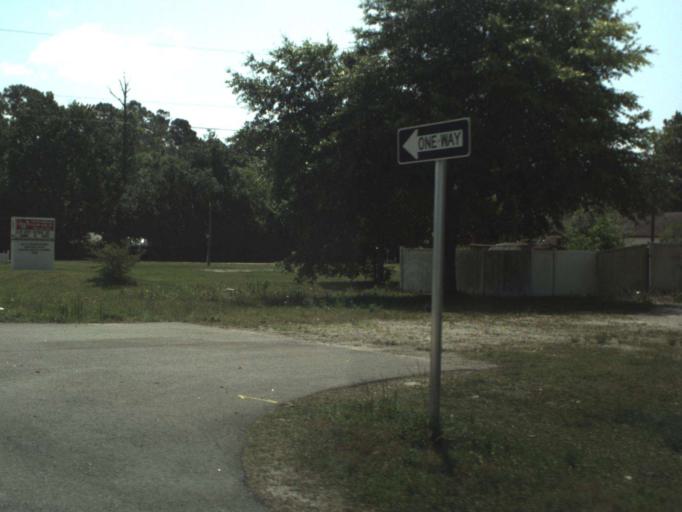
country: US
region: Florida
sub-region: Volusia County
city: Samsula-Spruce Creek
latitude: 29.1397
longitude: -81.1292
